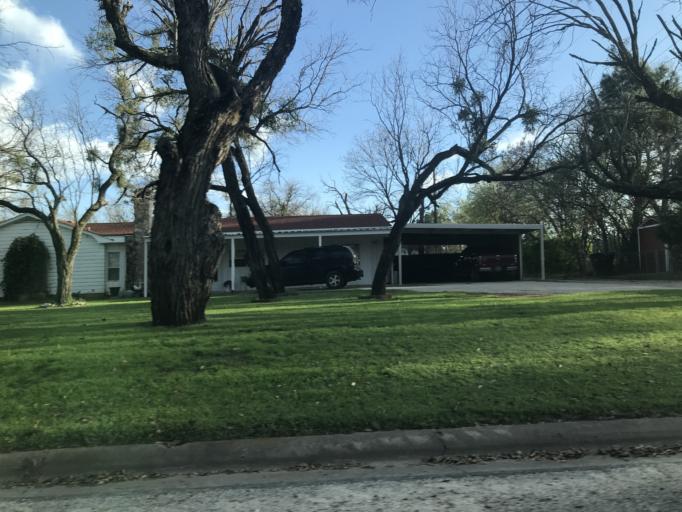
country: US
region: Texas
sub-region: Taylor County
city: Abilene
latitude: 32.4359
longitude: -99.7656
